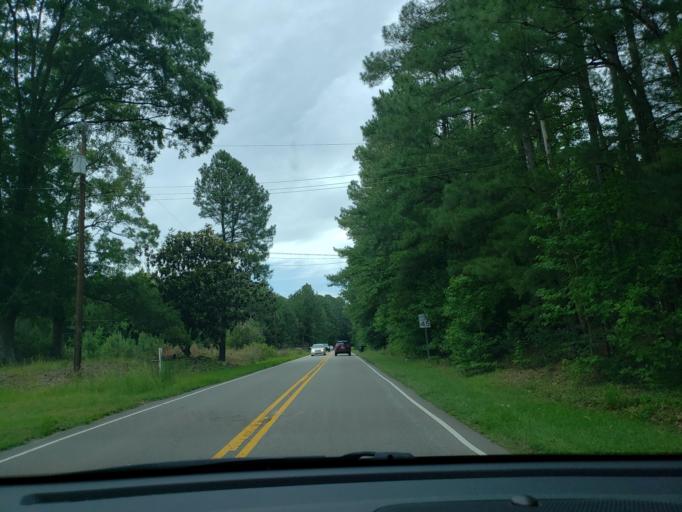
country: US
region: North Carolina
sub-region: Orange County
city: Chapel Hill
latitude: 35.8797
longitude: -78.9972
